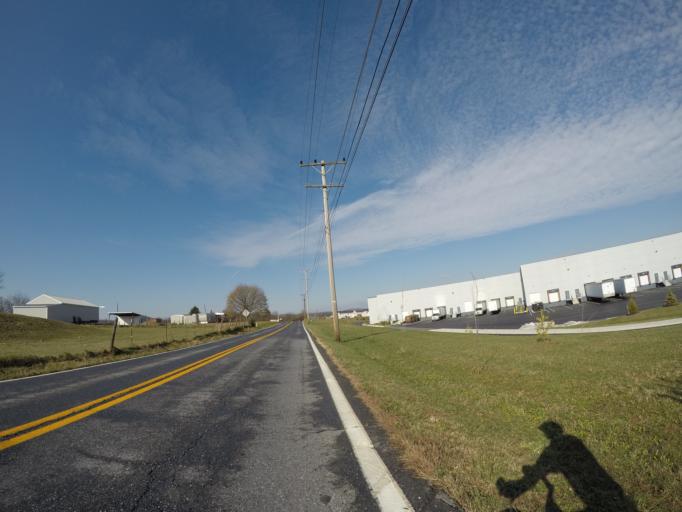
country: US
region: Maryland
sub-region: Frederick County
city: Ballenger Creek
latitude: 39.3617
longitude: -77.4445
